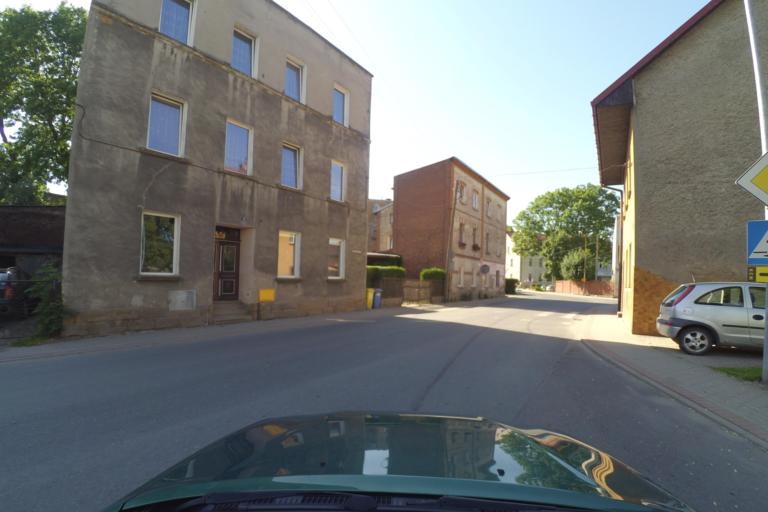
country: PL
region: Lower Silesian Voivodeship
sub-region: Powiat kamiennogorski
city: Lubawka
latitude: 50.7072
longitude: 15.9975
